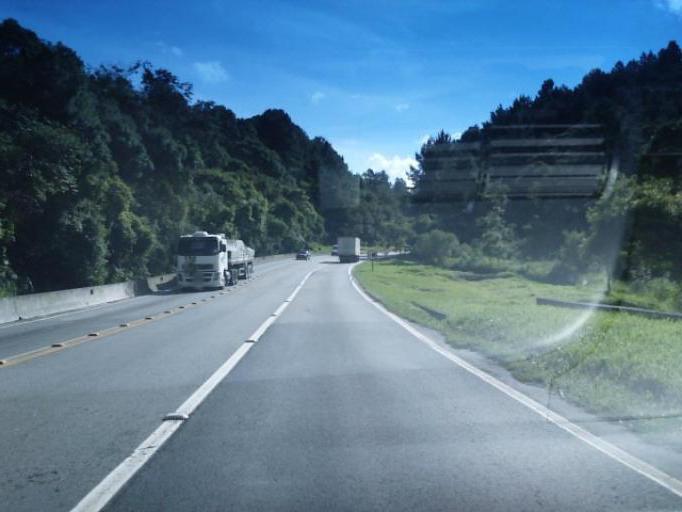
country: BR
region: Parana
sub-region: Campina Grande Do Sul
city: Campina Grande do Sul
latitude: -25.1812
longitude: -48.8821
